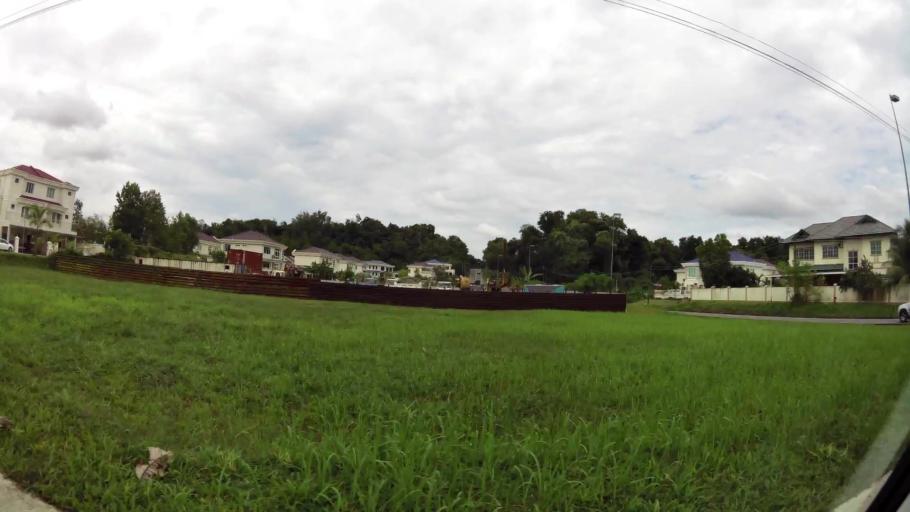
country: BN
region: Brunei and Muara
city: Bandar Seri Begawan
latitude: 4.8888
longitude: 114.9050
